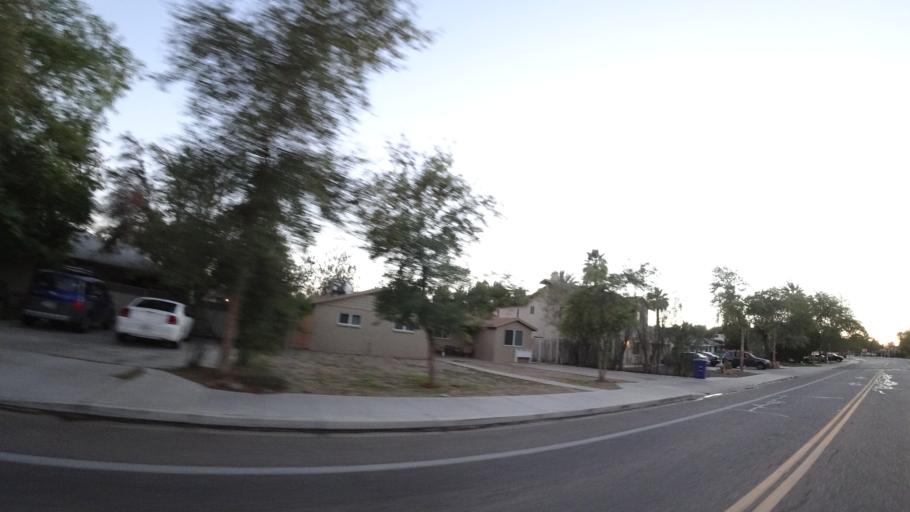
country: US
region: Arizona
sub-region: Maricopa County
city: Tempe Junction
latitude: 33.4146
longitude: -111.9465
